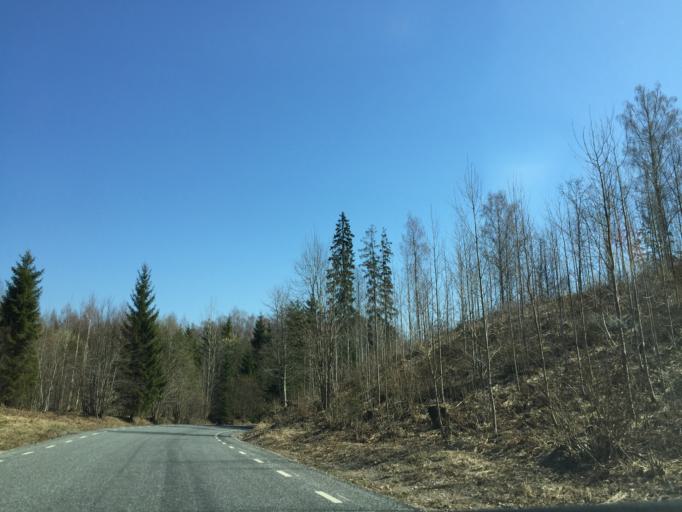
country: EE
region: Tartu
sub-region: Alatskivi vald
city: Kallaste
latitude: 58.5846
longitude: 27.0333
